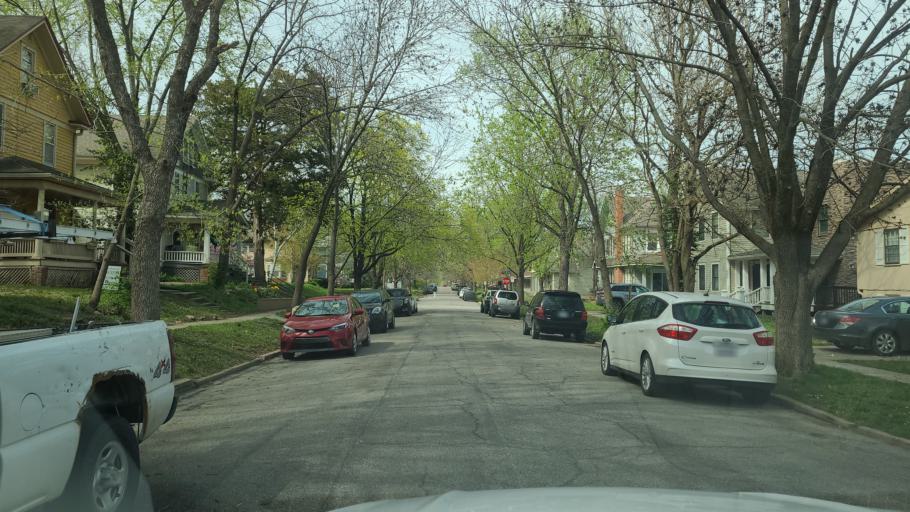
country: US
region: Kansas
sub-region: Douglas County
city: Lawrence
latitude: 38.9649
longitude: -95.2464
